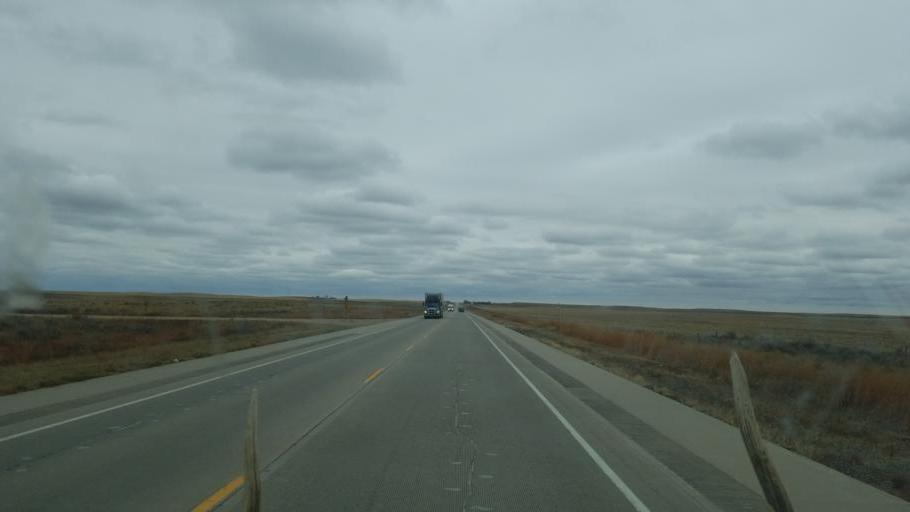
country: US
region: Colorado
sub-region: Kiowa County
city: Eads
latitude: 38.7055
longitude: -102.7758
